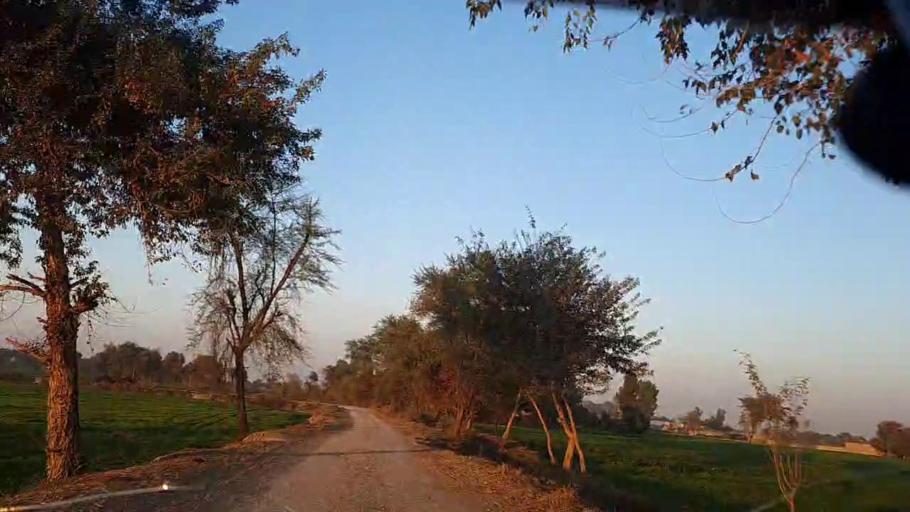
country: PK
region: Sindh
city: Adilpur
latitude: 27.8377
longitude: 69.2987
